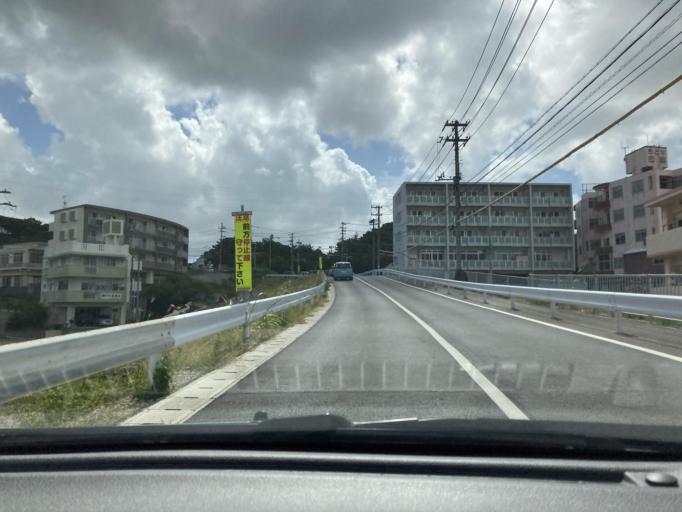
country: JP
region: Okinawa
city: Ginowan
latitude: 26.2584
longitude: 127.7252
